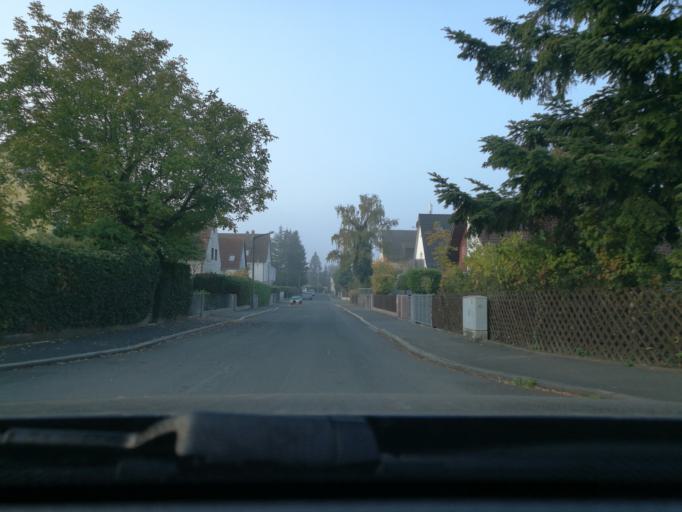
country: DE
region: Bavaria
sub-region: Regierungsbezirk Mittelfranken
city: Furth
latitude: 49.4880
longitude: 10.9630
